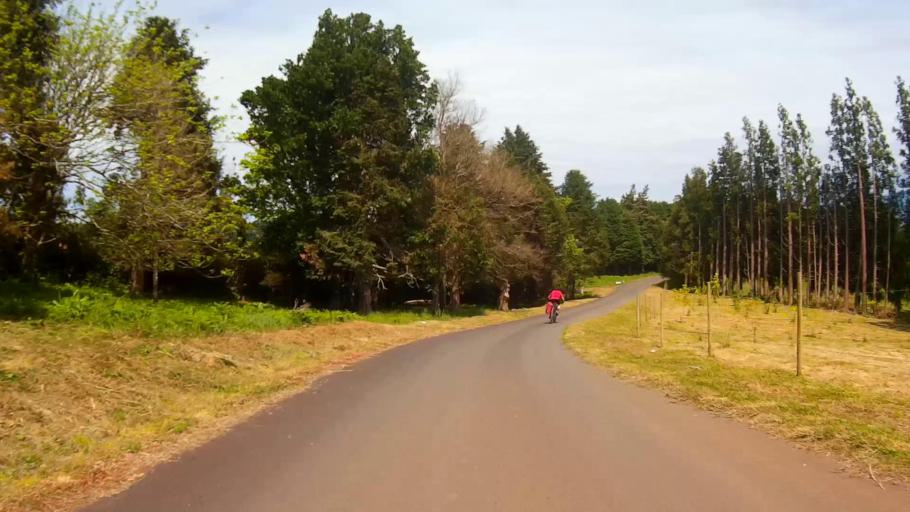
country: PT
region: Azores
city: Ribeira Grande
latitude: 38.5527
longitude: -28.6755
